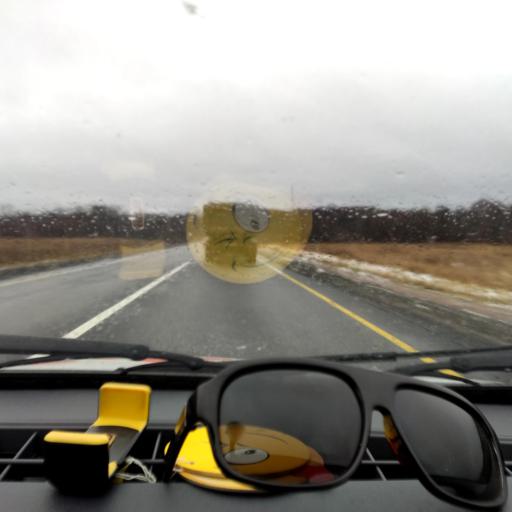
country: RU
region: Bashkortostan
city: Urman
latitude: 54.8175
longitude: 56.8595
